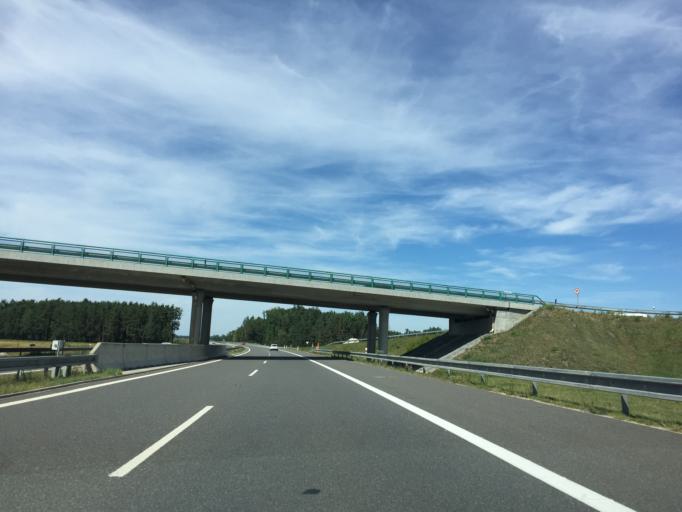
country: CZ
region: Jihocesky
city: Sobeslav
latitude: 49.2228
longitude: 14.7277
